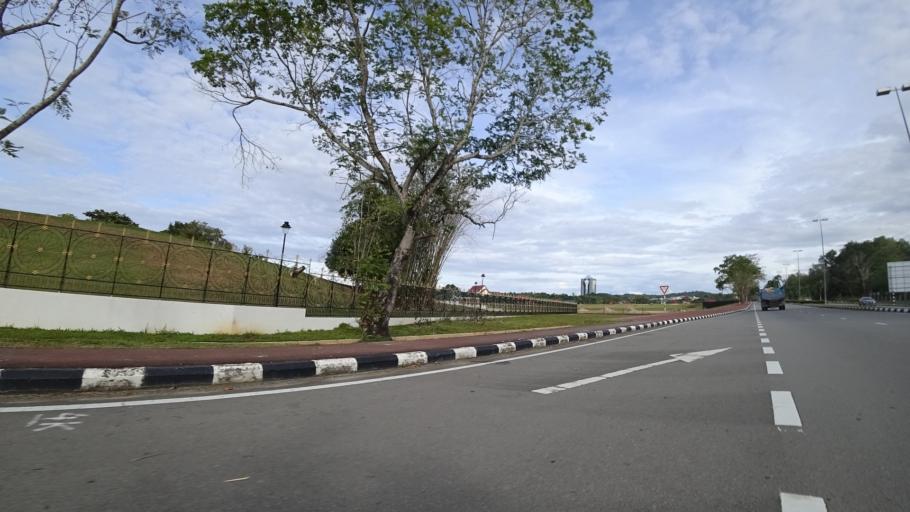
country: BN
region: Brunei and Muara
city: Bandar Seri Begawan
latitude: 4.9230
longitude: 114.9385
